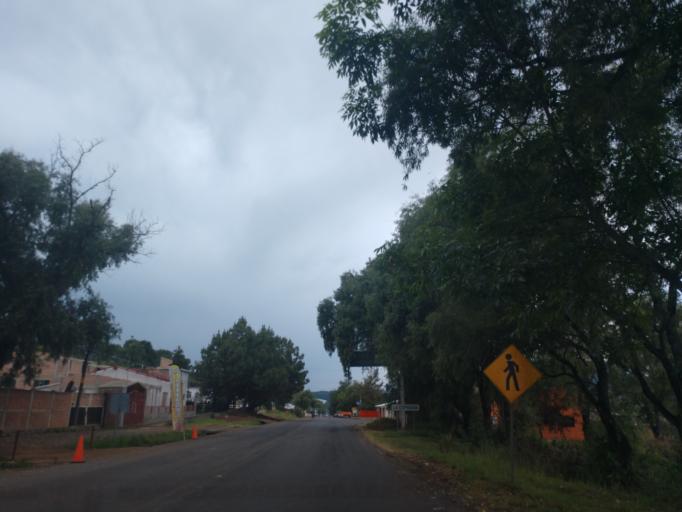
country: MX
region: Jalisco
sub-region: Mazamitla
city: Mazamitla
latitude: 19.9235
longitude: -103.0437
